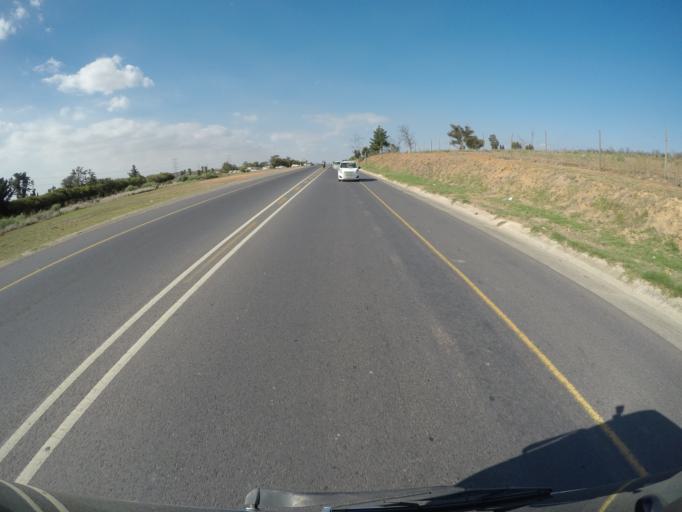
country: ZA
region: Western Cape
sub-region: City of Cape Town
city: Kraaifontein
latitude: -33.8886
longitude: 18.7445
